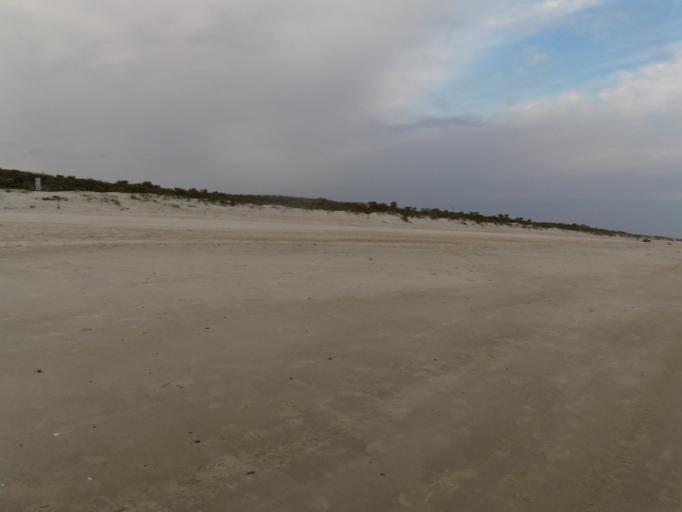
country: US
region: Florida
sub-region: Duval County
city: Atlantic Beach
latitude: 30.3604
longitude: -81.3972
